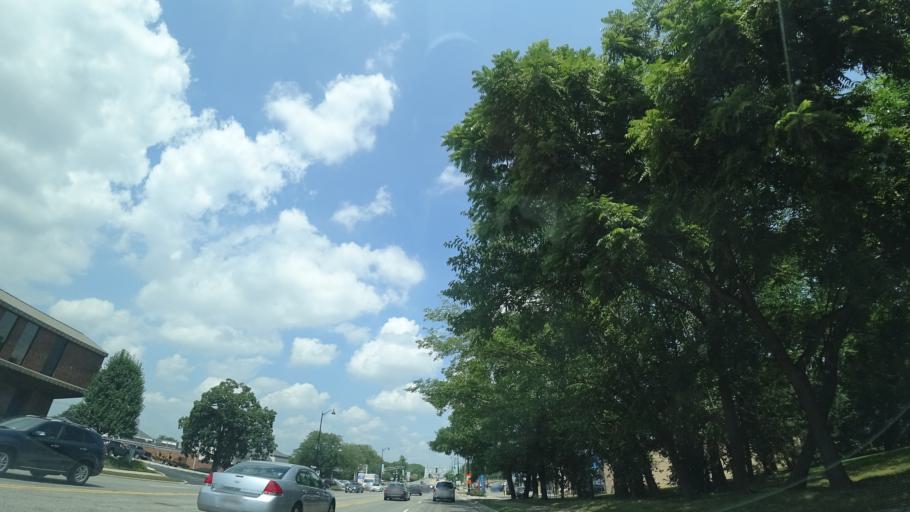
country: US
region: Illinois
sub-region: Cook County
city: Palos Heights
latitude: 41.6739
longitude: -87.7967
